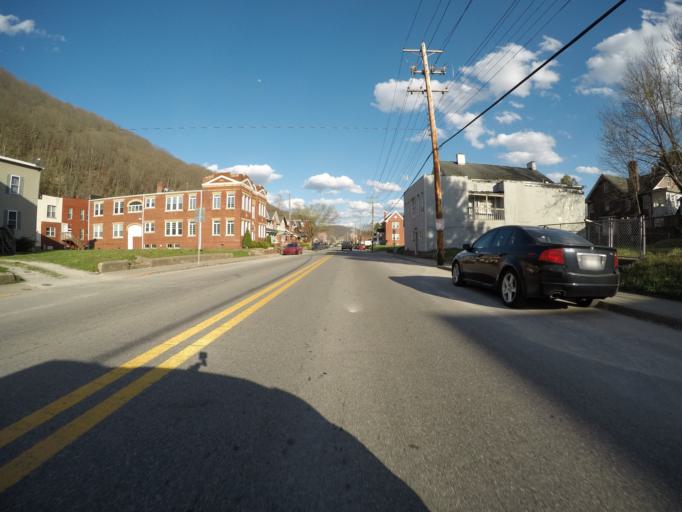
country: US
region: West Virginia
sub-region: Kanawha County
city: Charleston
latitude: 38.3363
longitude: -81.6066
